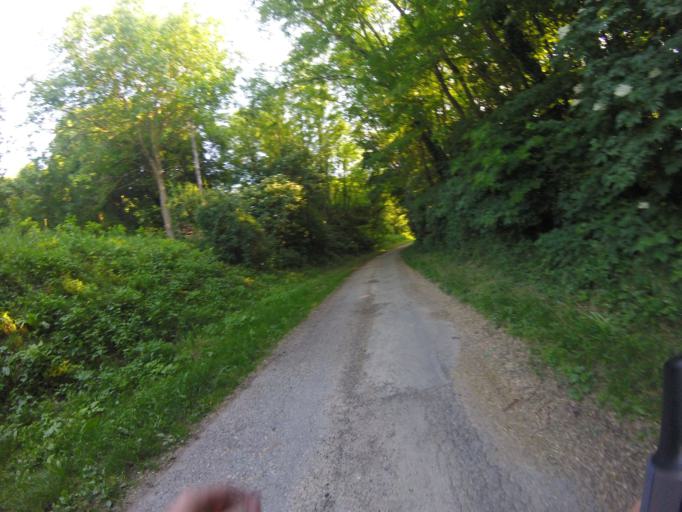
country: HU
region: Zala
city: Zalaszentgrot
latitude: 46.8765
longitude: 17.1313
